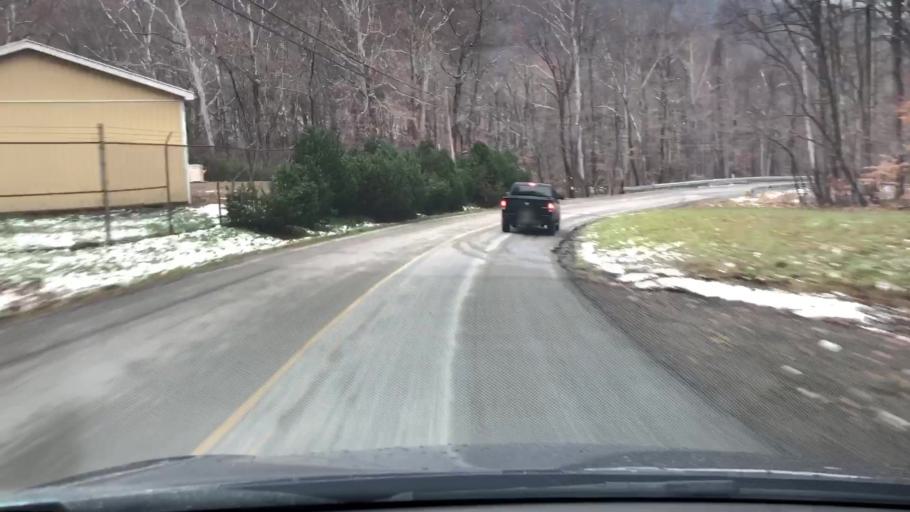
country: US
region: Pennsylvania
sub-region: Fayette County
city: Dunbar
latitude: 39.9440
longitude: -79.5787
